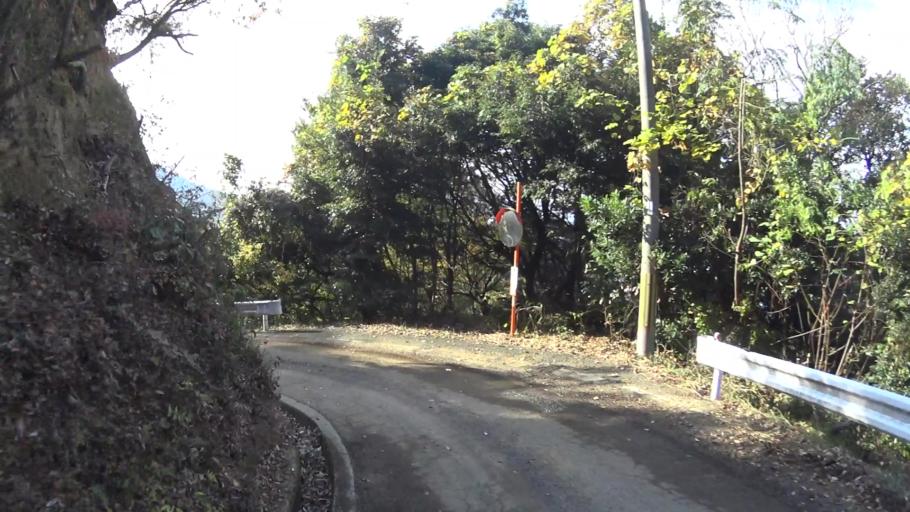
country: JP
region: Kyoto
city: Maizuru
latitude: 35.5615
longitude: 135.4073
